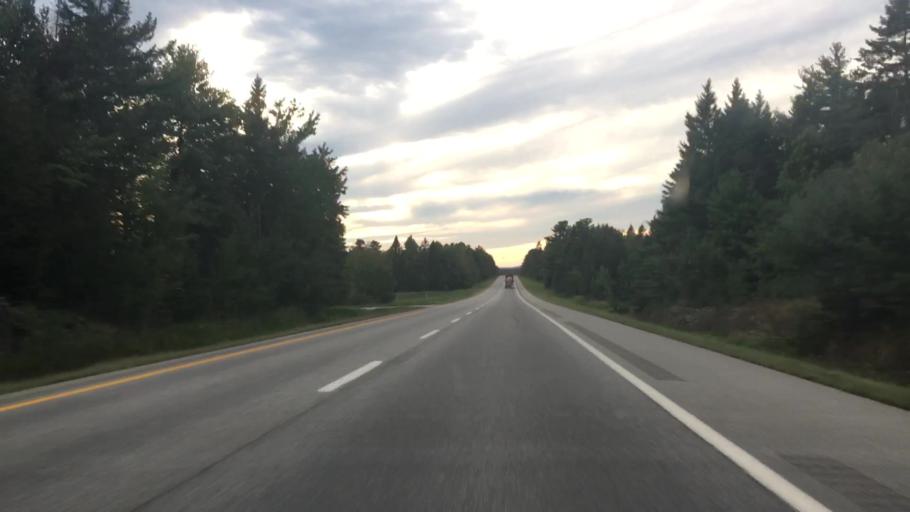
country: US
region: Maine
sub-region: Penobscot County
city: Plymouth
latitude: 44.7885
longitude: -69.1676
